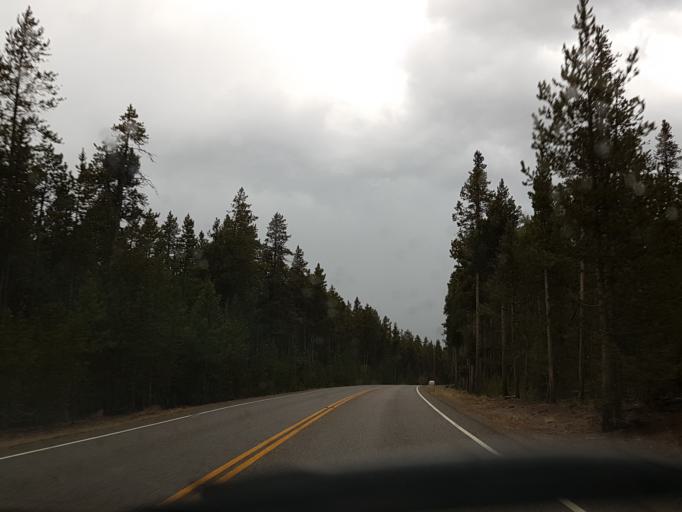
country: US
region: Montana
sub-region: Gallatin County
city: West Yellowstone
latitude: 44.4624
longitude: -110.5133
